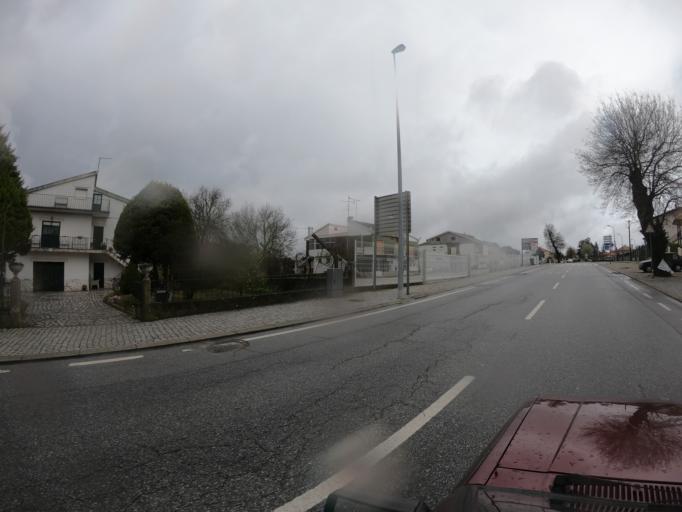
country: PT
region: Guarda
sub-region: Celorico da Beira
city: Celorico da Beira
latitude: 40.6274
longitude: -7.4002
